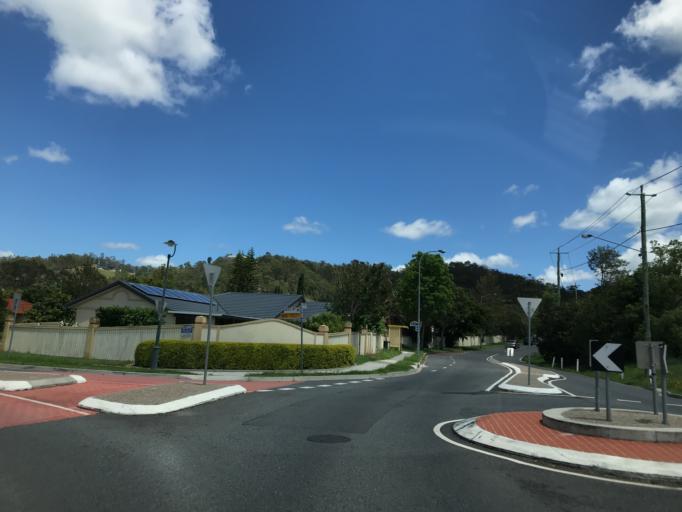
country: AU
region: Queensland
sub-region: Brisbane
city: Kenmore Hills
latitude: -27.4519
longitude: 152.9356
